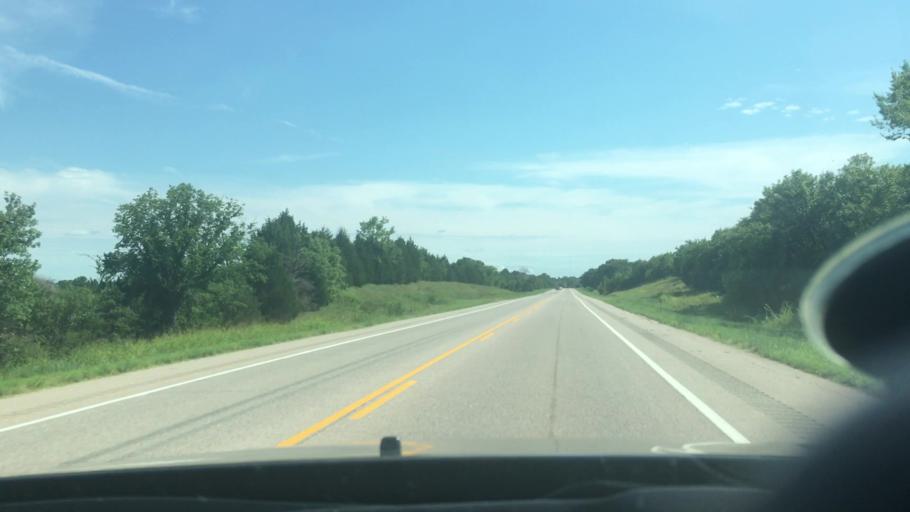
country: US
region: Oklahoma
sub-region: Seminole County
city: Konawa
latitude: 34.9656
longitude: -96.6789
